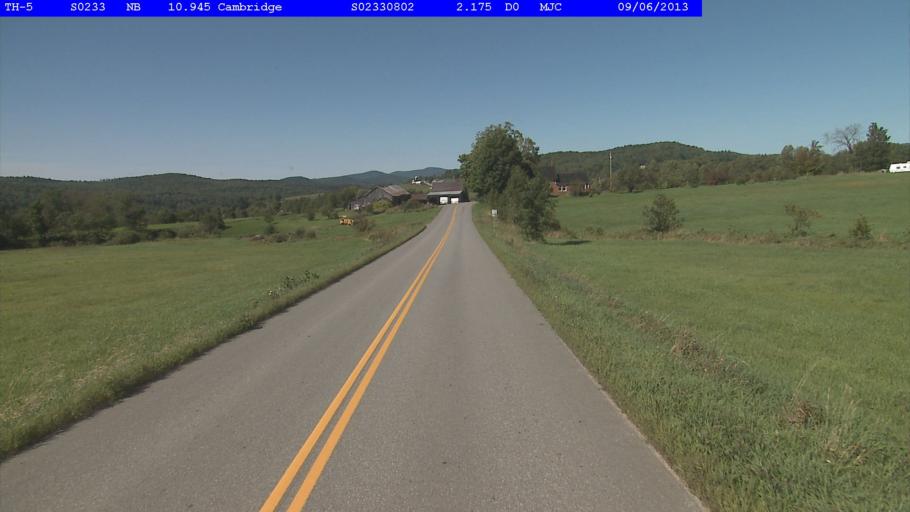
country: US
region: Vermont
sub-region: Chittenden County
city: Jericho
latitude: 44.6131
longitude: -72.8572
